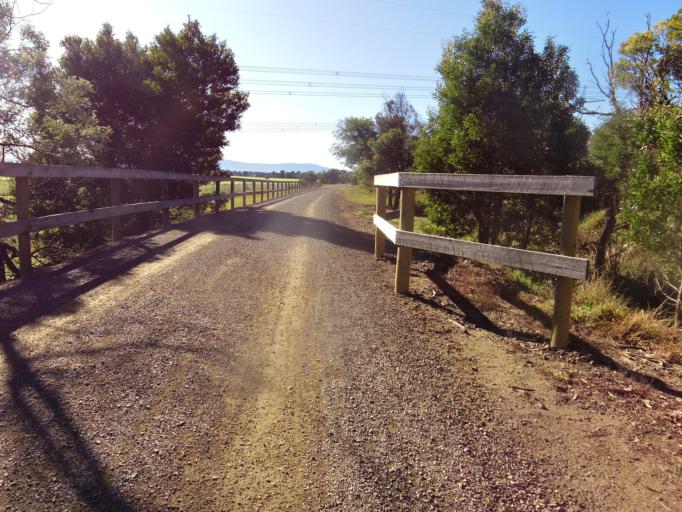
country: AU
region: Victoria
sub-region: Yarra Ranges
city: Lilydale
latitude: -37.7354
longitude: 145.3648
